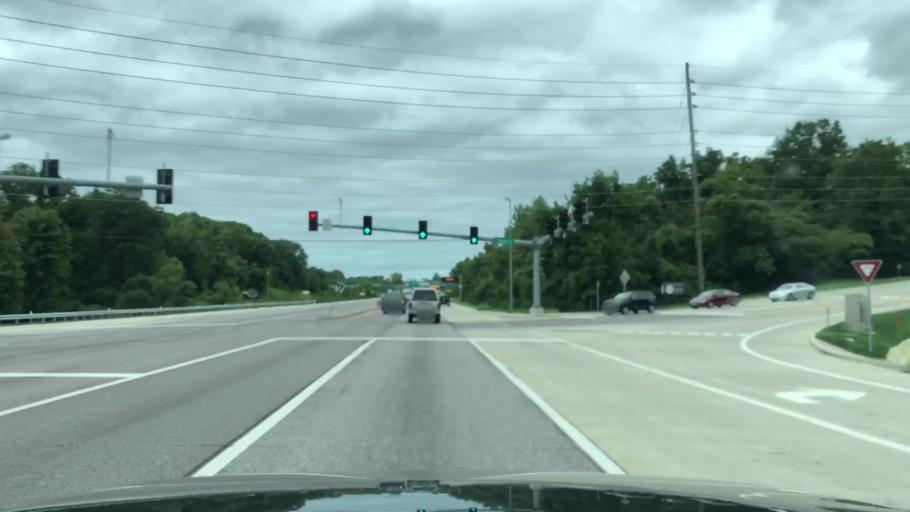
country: US
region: Missouri
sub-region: Saint Louis County
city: Manchester
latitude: 38.6497
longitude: -90.5077
